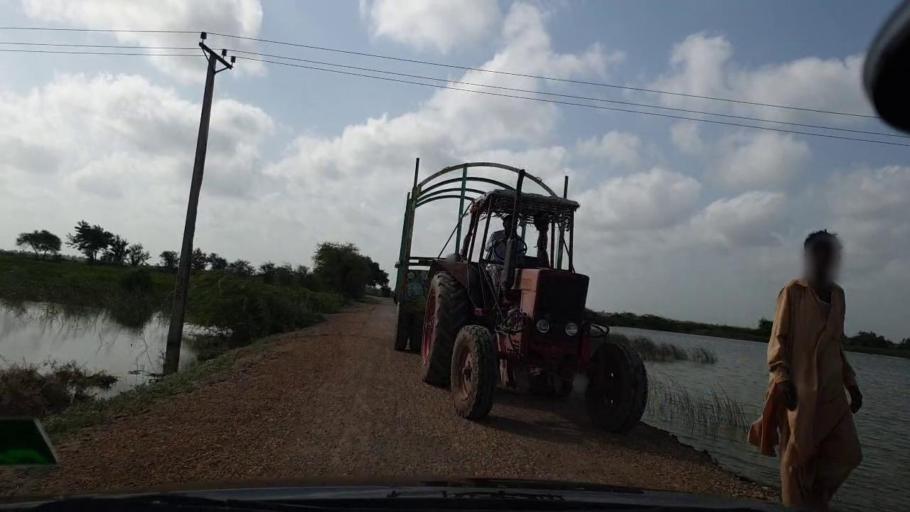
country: PK
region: Sindh
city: Kadhan
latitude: 24.6393
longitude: 69.0870
